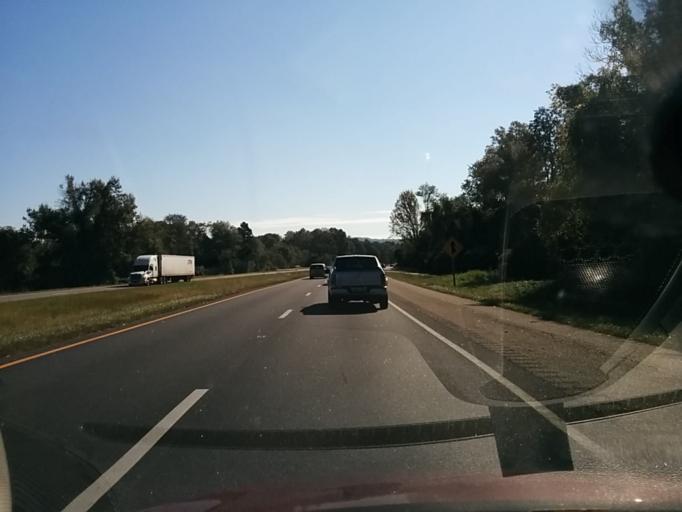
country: US
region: Virginia
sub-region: City of Charlottesville
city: Charlottesville
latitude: 38.0217
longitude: -78.5400
